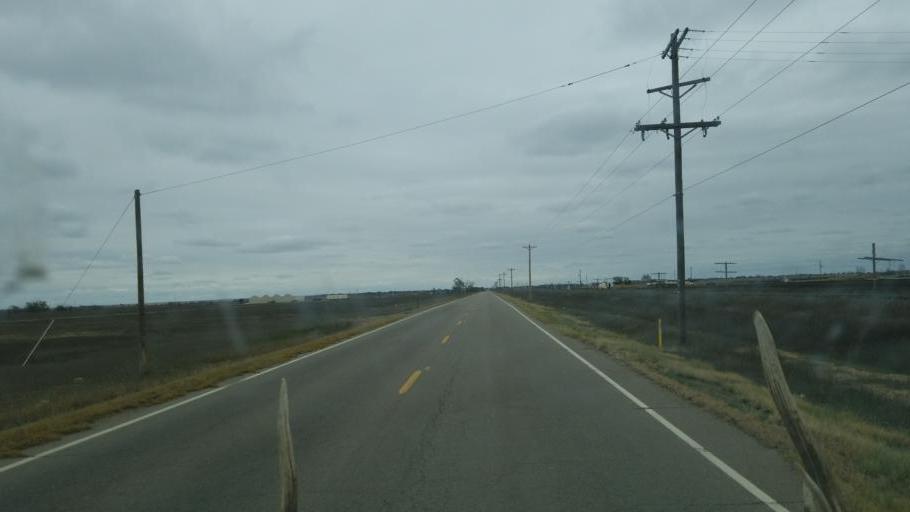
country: US
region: Colorado
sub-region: Crowley County
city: Ordway
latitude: 38.2234
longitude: -103.7178
